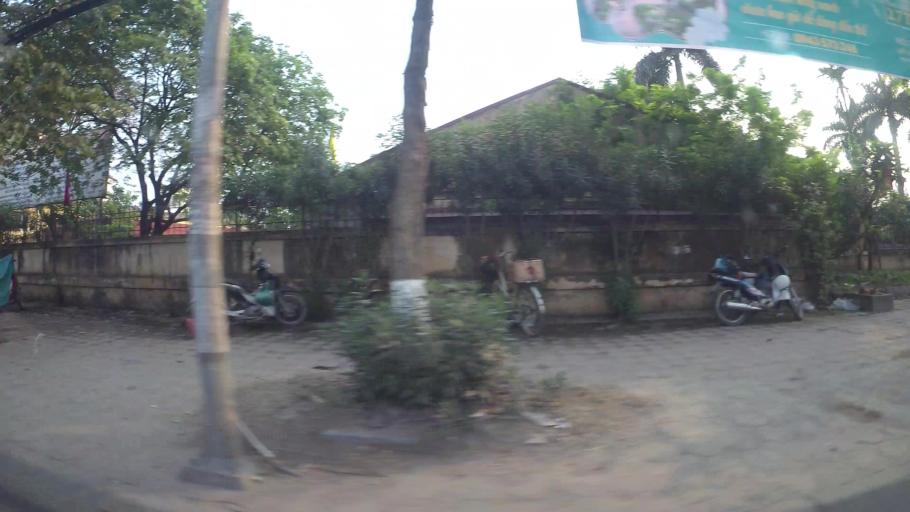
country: VN
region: Ha Noi
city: Thanh Xuan
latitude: 20.9781
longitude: 105.8231
